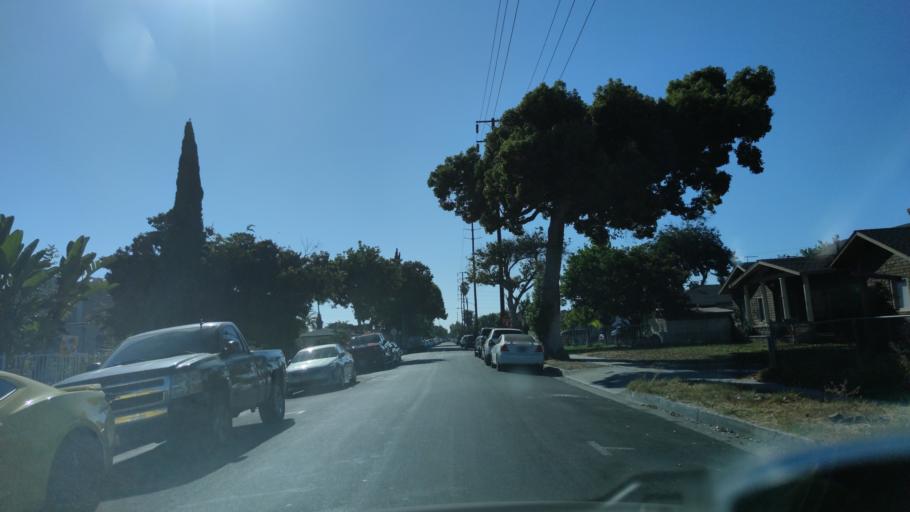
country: US
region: California
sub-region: Los Angeles County
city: Maywood
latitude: 33.9911
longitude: -118.1955
